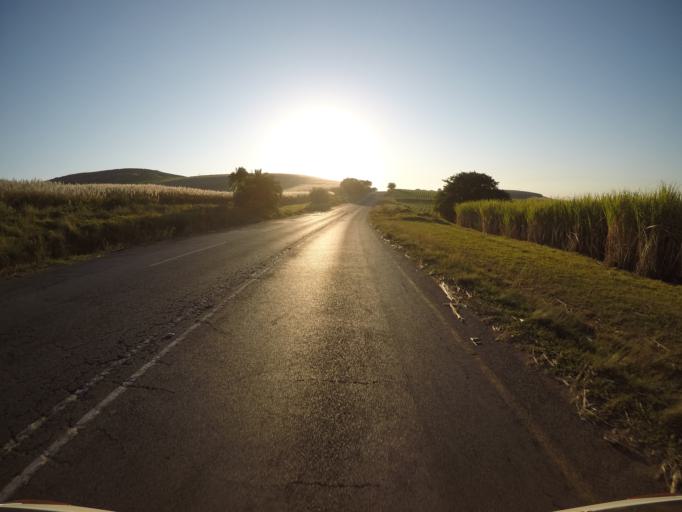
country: ZA
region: KwaZulu-Natal
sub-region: uThungulu District Municipality
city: Eshowe
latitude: -28.9503
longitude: 31.6720
